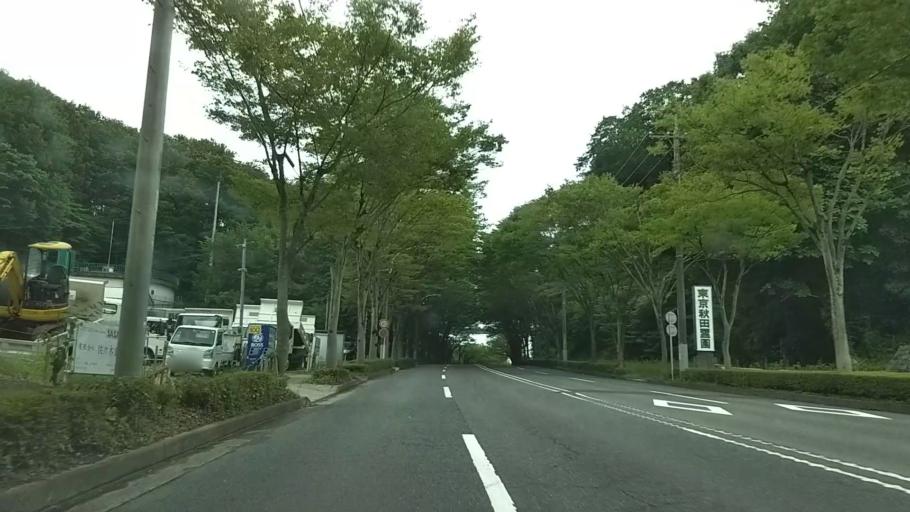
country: JP
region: Tokyo
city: Hachioji
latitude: 35.6172
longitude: 139.2968
